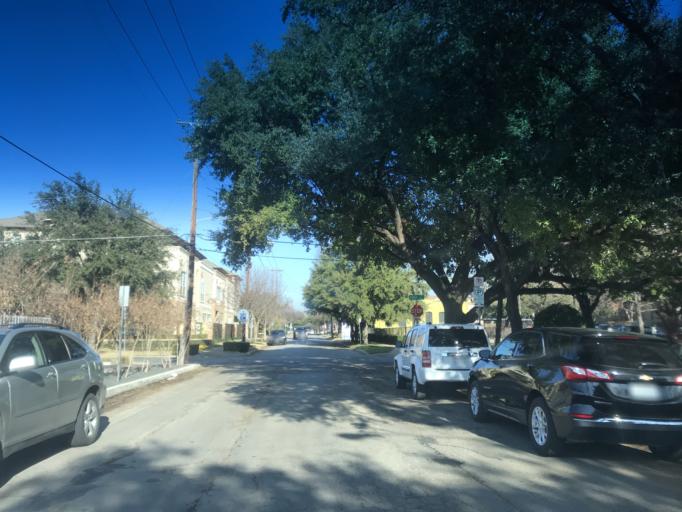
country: US
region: Texas
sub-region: Dallas County
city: Dallas
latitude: 32.8108
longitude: -96.8092
